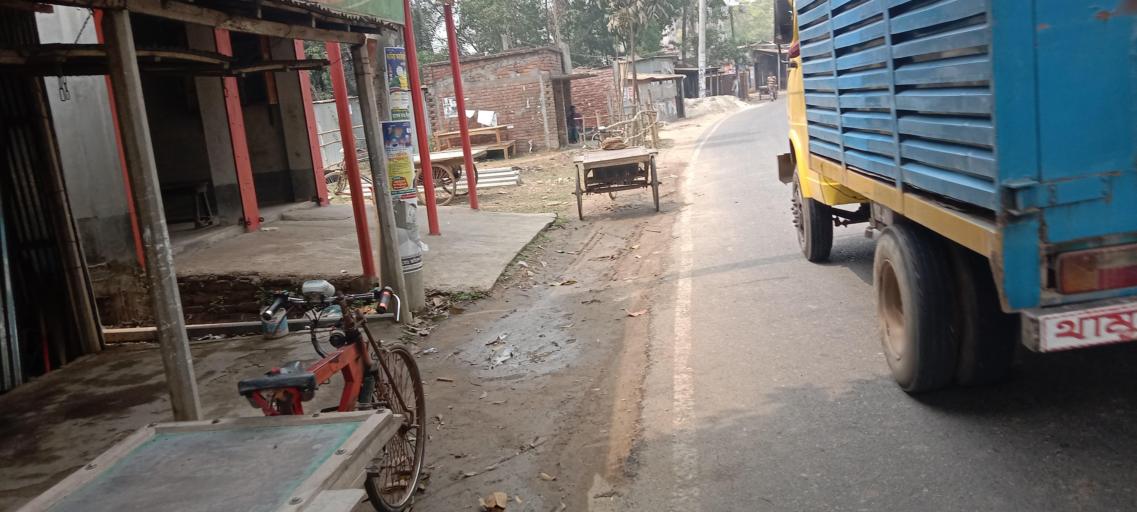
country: BD
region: Dhaka
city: Sakhipur
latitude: 24.4444
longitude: 90.3408
